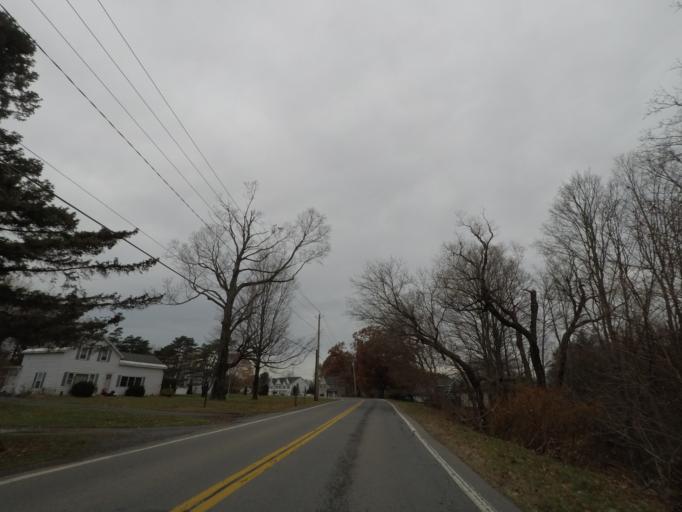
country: US
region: New York
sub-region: Saratoga County
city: Waterford
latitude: 42.8466
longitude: -73.6860
